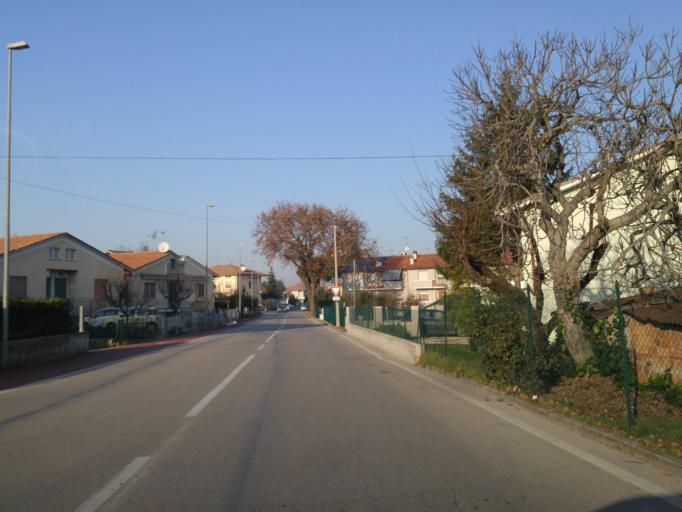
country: IT
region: The Marches
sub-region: Provincia di Pesaro e Urbino
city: Lucrezia
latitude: 43.7755
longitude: 12.9420
